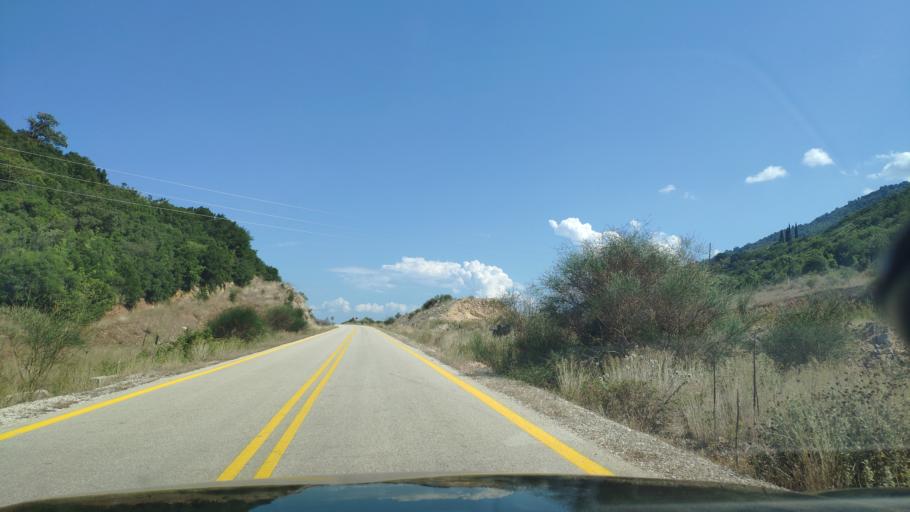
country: GR
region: West Greece
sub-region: Nomos Aitolias kai Akarnanias
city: Katouna
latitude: 38.8558
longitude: 21.0872
